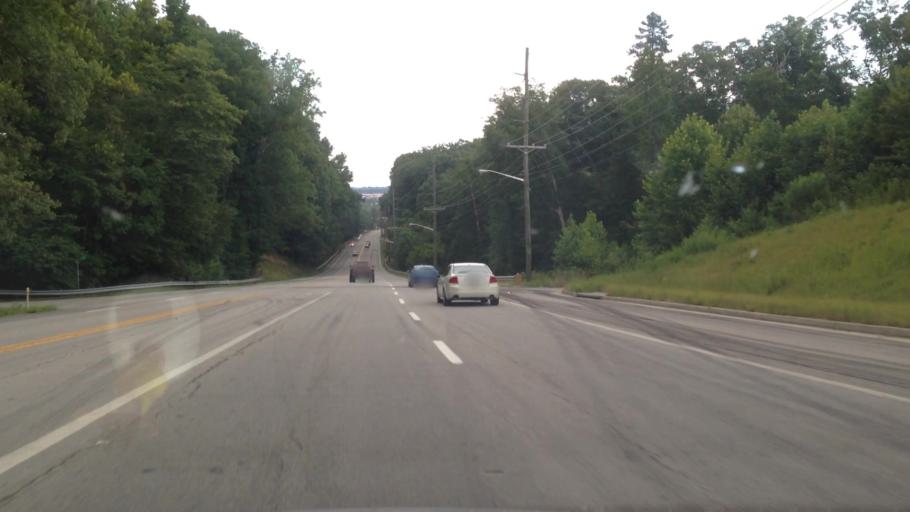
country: US
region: Virginia
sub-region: City of Danville
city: Danville
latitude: 36.5673
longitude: -79.4389
